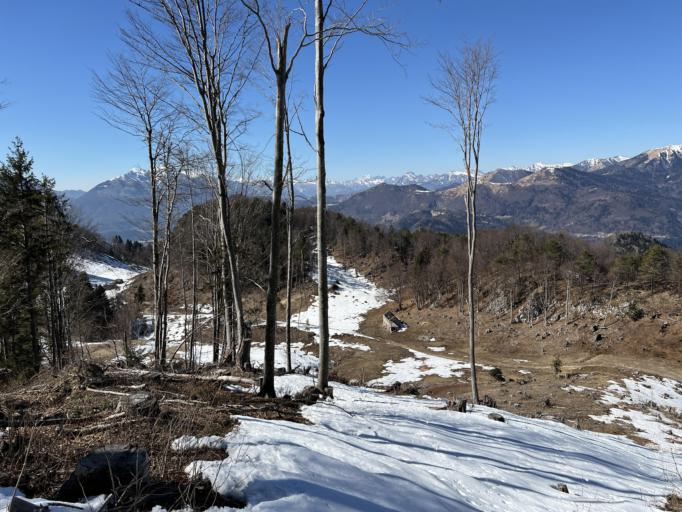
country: IT
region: Friuli Venezia Giulia
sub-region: Provincia di Udine
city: Zuglio
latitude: 46.4491
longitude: 13.0801
